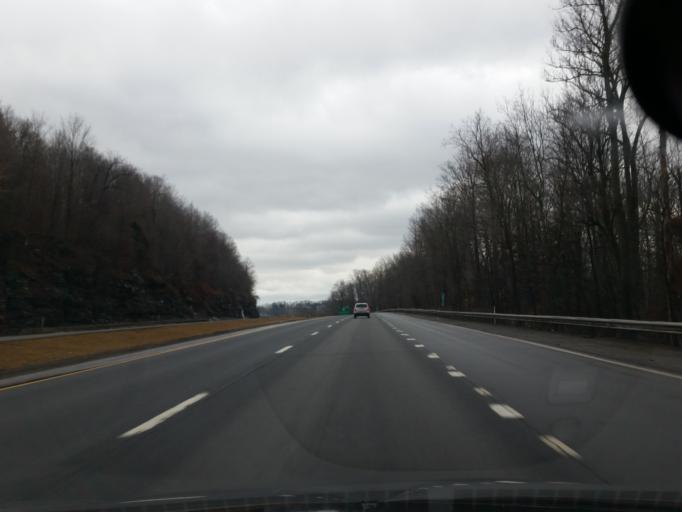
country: US
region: Pennsylvania
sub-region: Lackawanna County
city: Dalton
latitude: 41.5896
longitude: -75.6527
